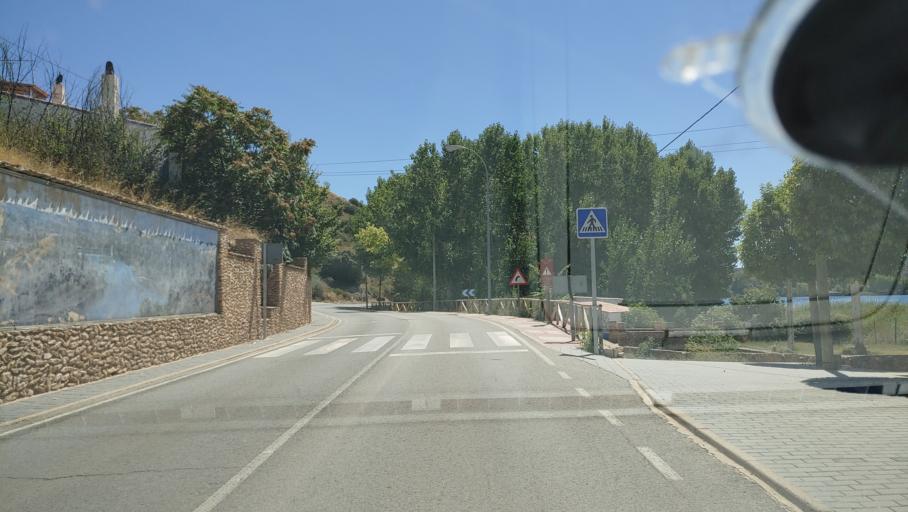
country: ES
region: Castille-La Mancha
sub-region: Provincia de Ciudad Real
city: Ruidera
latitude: 38.9738
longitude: -2.8863
